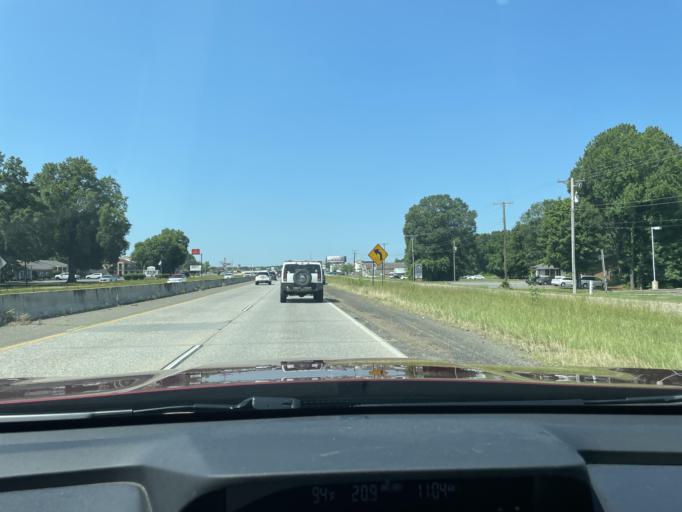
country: US
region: Arkansas
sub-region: Pulaski County
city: Jacksonville
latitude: 34.8721
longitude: -92.1226
